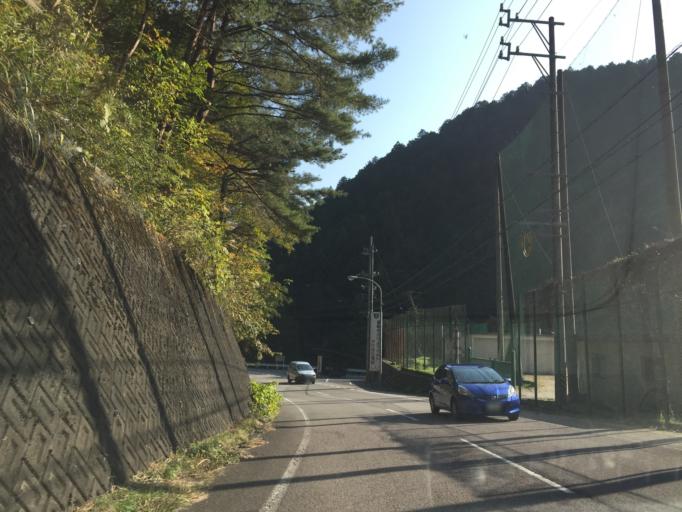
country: JP
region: Gifu
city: Minokamo
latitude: 35.5564
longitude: 137.1110
